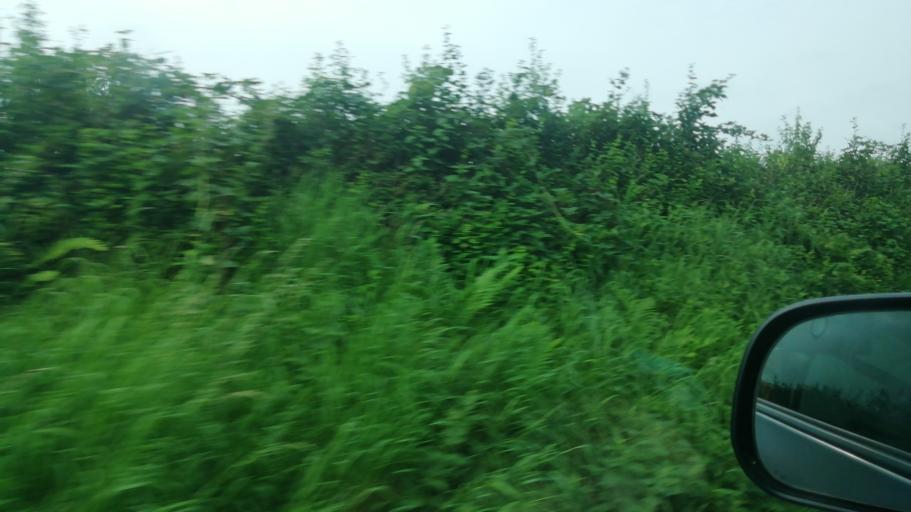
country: IE
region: Munster
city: Fethard
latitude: 52.5609
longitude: -7.5704
